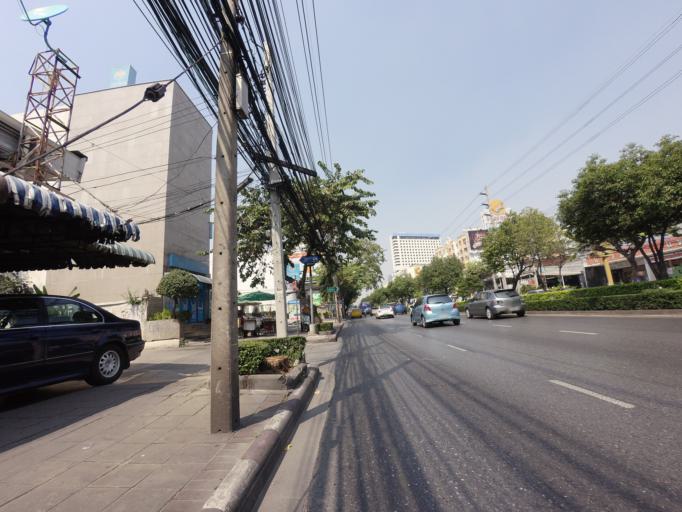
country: TH
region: Bangkok
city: Wang Thonglang
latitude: 13.7830
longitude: 100.6146
